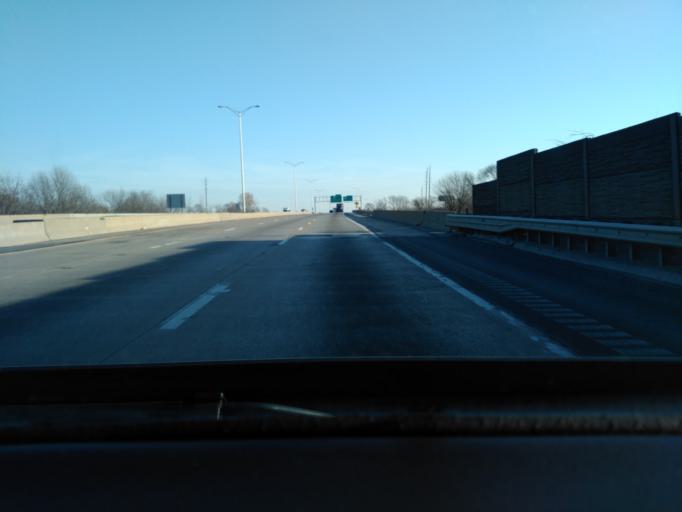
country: US
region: Illinois
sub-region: Saint Clair County
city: Centreville
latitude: 38.5770
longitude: -90.1150
